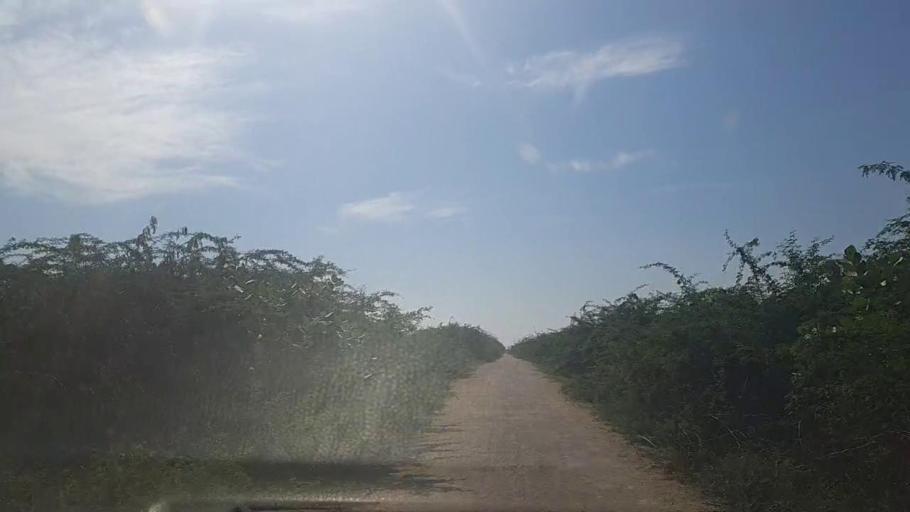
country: PK
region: Sindh
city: Mirpur Batoro
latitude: 24.6762
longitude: 68.1827
